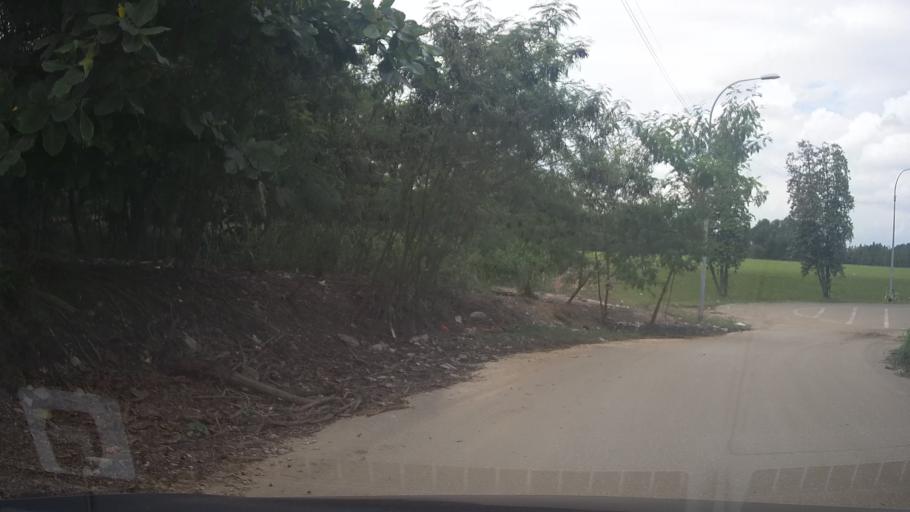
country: MY
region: Johor
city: Kampung Pasir Gudang Baru
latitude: 1.3850
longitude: 103.9346
